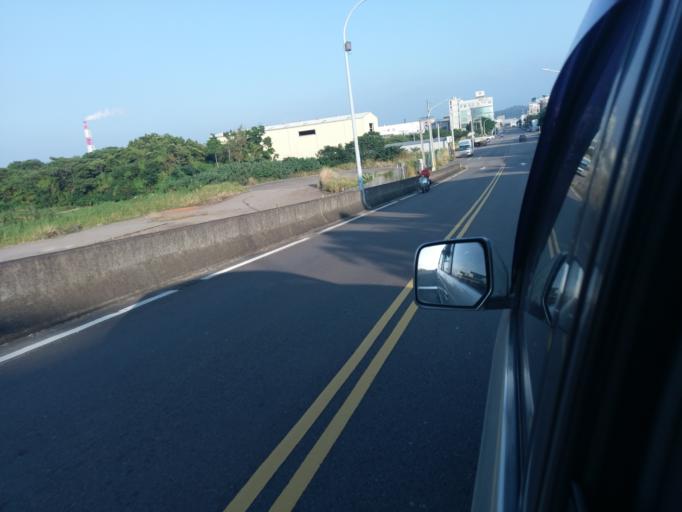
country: TW
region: Taiwan
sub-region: Miaoli
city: Miaoli
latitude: 24.6753
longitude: 120.8814
